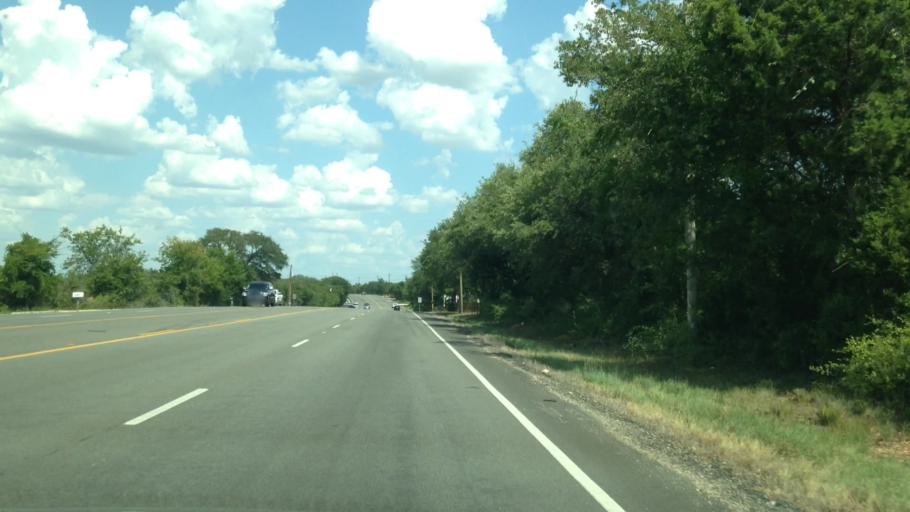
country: US
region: Texas
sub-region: Williamson County
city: Georgetown
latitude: 30.6313
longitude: -97.7498
